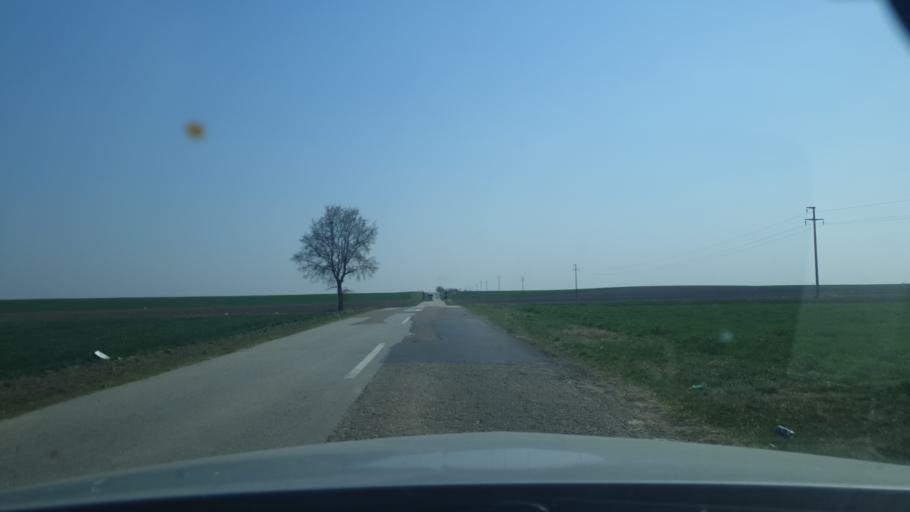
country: RS
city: Sasinci
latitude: 45.0392
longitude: 19.7351
